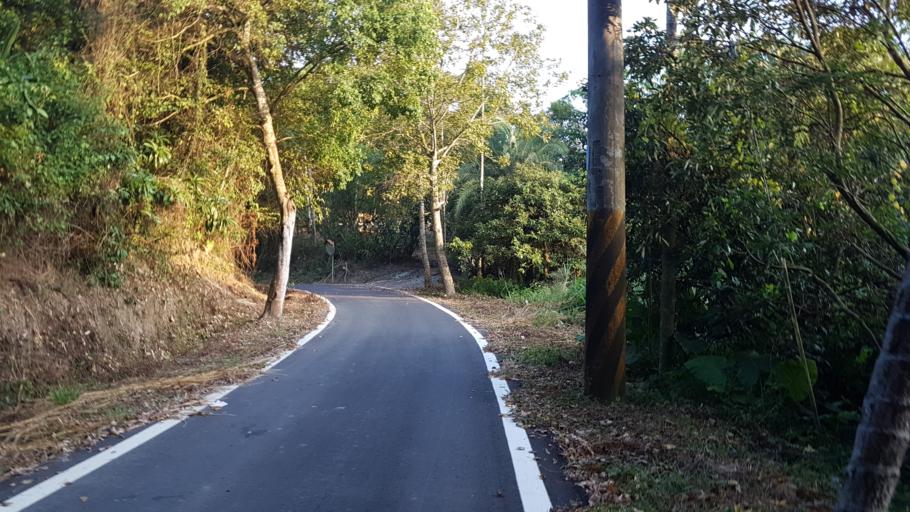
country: TW
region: Taiwan
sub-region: Chiayi
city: Jiayi Shi
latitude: 23.3624
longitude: 120.4659
